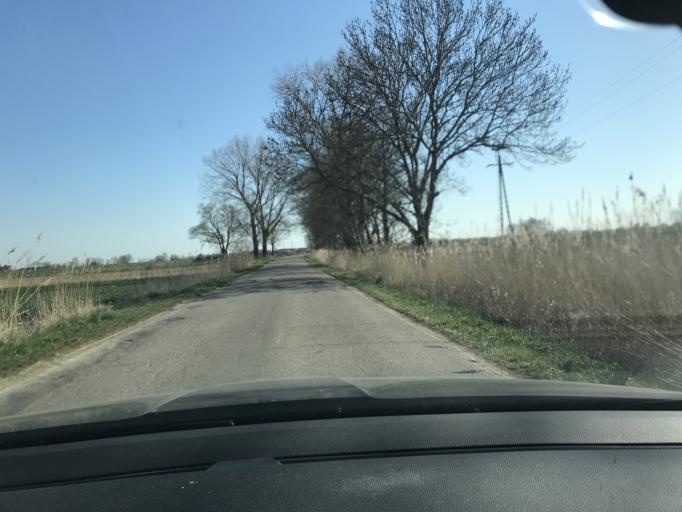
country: PL
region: Pomeranian Voivodeship
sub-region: Powiat nowodworski
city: Sztutowo
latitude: 54.3242
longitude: 19.1573
